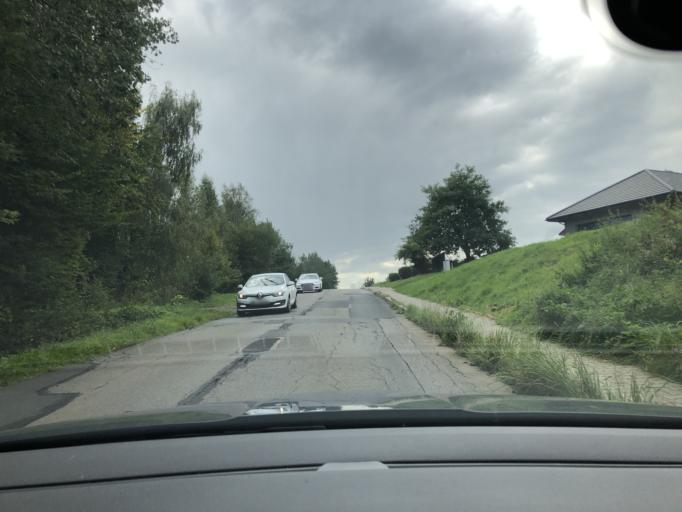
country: PL
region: Silesian Voivodeship
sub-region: Powiat zywiecki
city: Zarzecze
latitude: 49.7252
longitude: 19.1803
